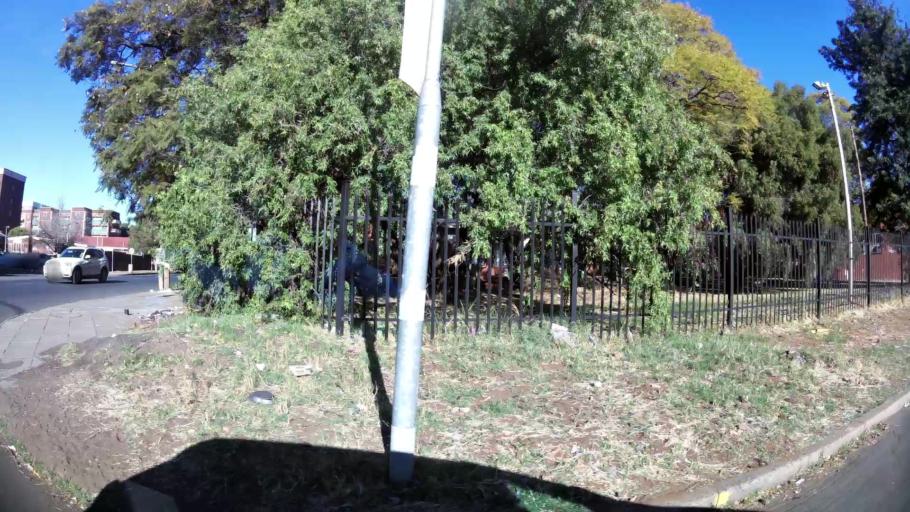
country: ZA
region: Northern Cape
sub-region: Frances Baard District Municipality
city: Kimberley
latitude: -28.7451
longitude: 24.7709
